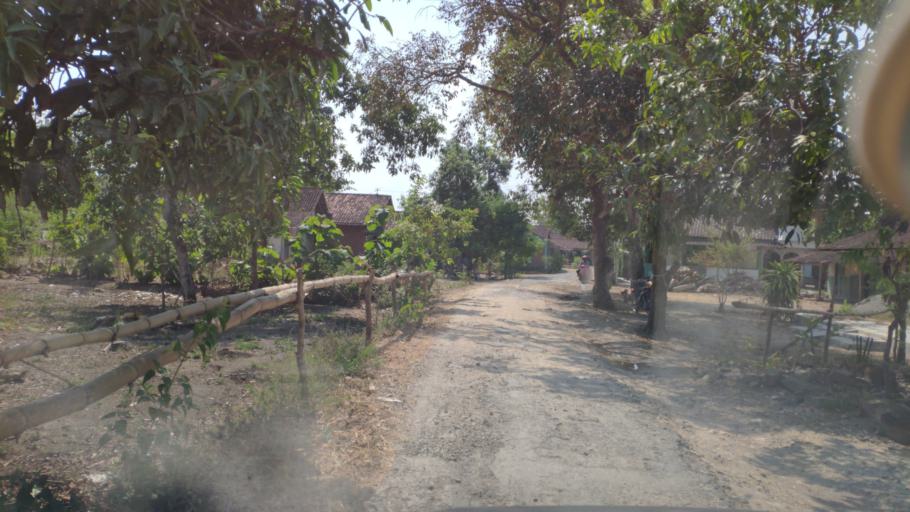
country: ID
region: Central Java
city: Botoh
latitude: -7.0932
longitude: 111.4744
